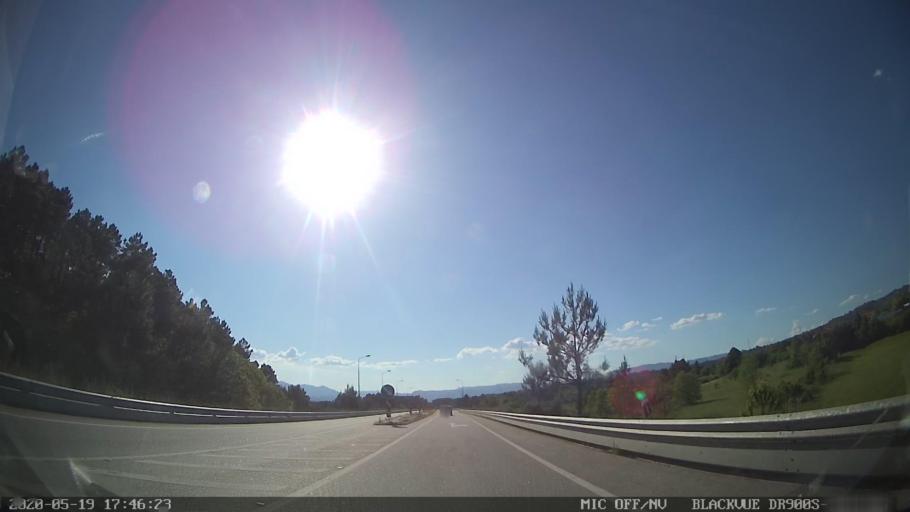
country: PT
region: Vila Real
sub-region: Sabrosa
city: Vilela
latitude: 41.2660
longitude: -7.6320
